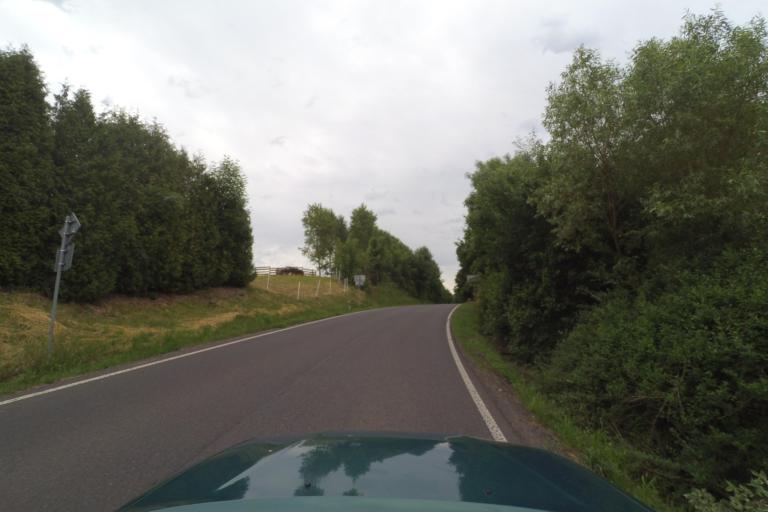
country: CZ
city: Cesky Dub
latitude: 50.6732
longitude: 14.9922
